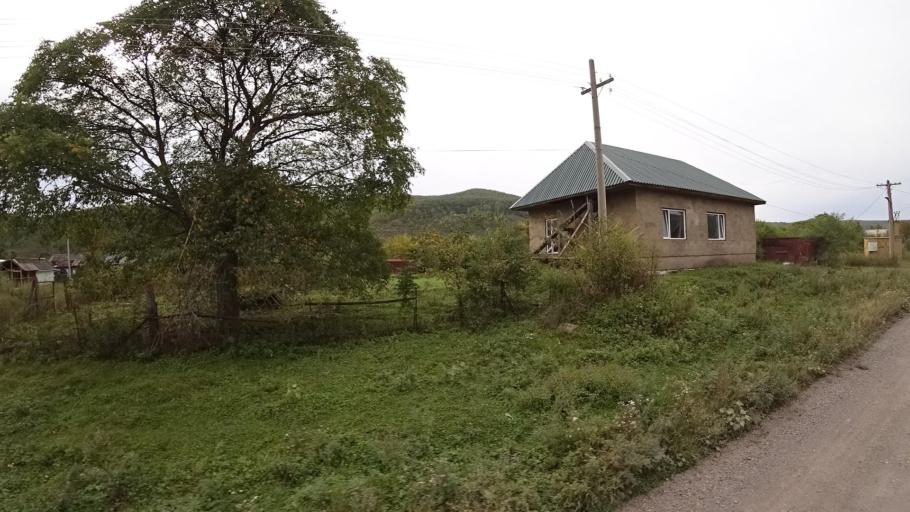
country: RU
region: Jewish Autonomous Oblast
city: Khingansk
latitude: 49.0355
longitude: 131.0494
